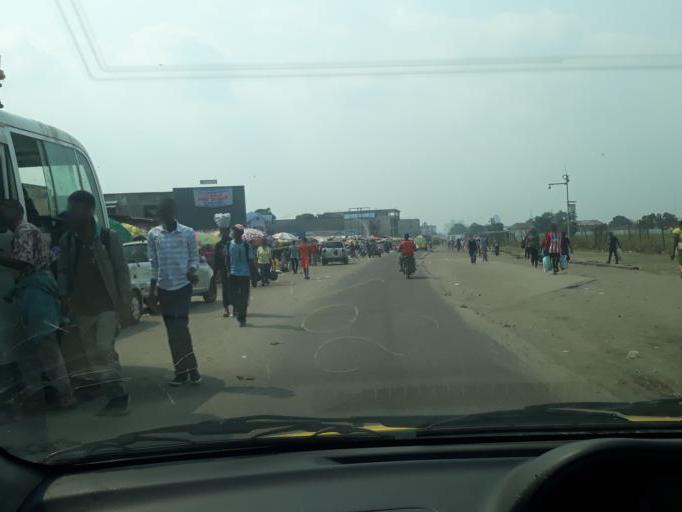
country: CD
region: Kinshasa
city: Kinshasa
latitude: -4.3302
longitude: 15.3202
